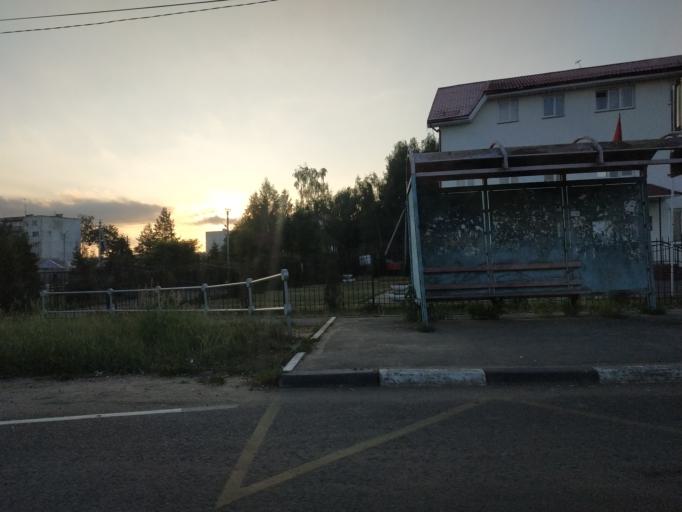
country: RU
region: Moskovskaya
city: Krasnoarmeysk
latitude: 56.0619
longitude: 38.2551
